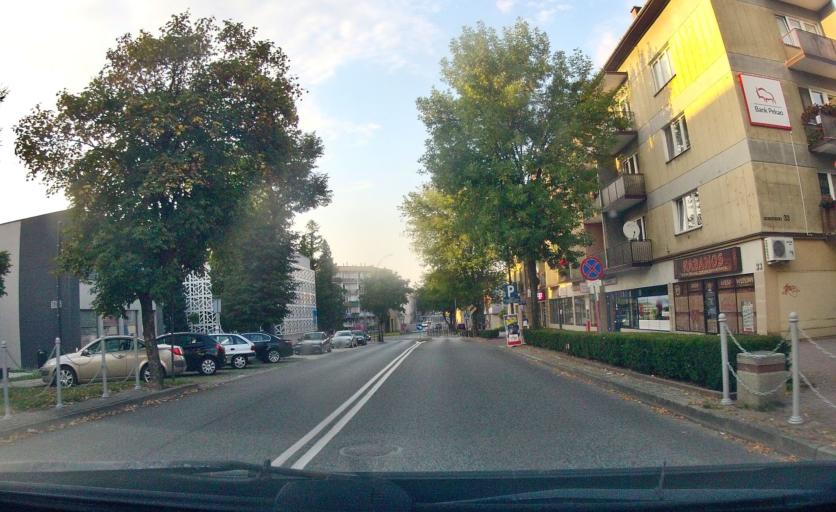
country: PL
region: Subcarpathian Voivodeship
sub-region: Powiat jasielski
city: Jaslo
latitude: 49.7438
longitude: 21.4735
